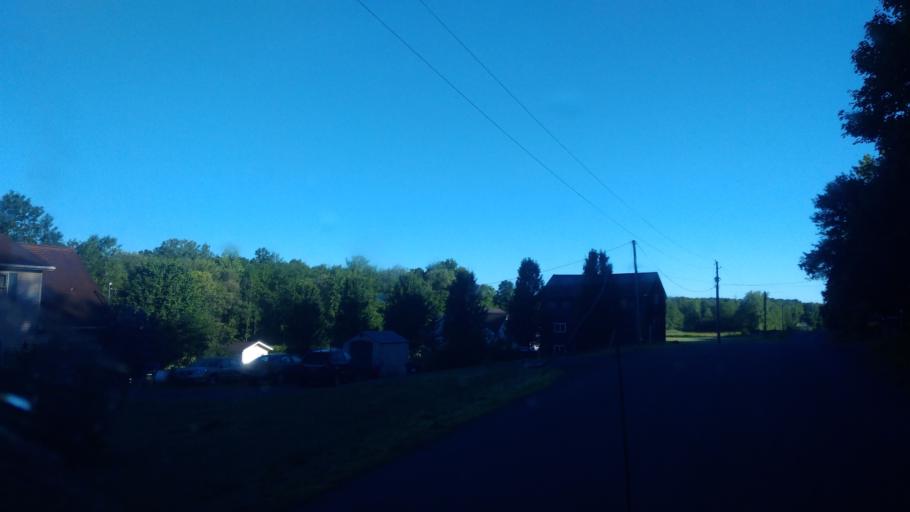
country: US
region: New York
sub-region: Wayne County
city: Lyons
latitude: 43.1409
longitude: -77.0425
